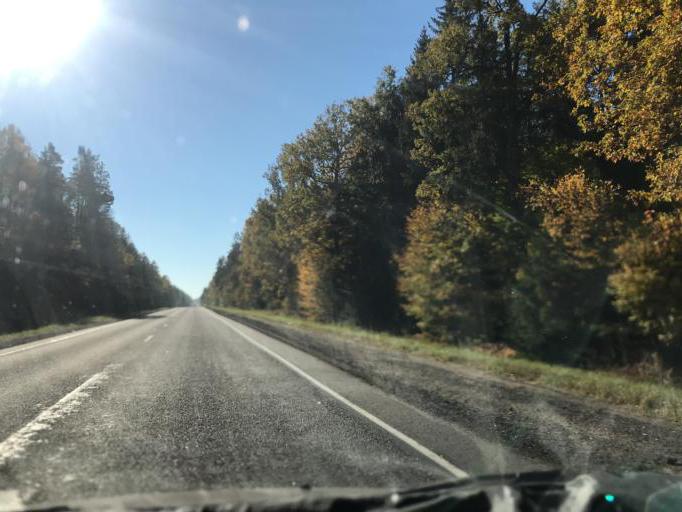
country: BY
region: Mogilev
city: Babruysk
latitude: 53.1401
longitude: 29.0493
